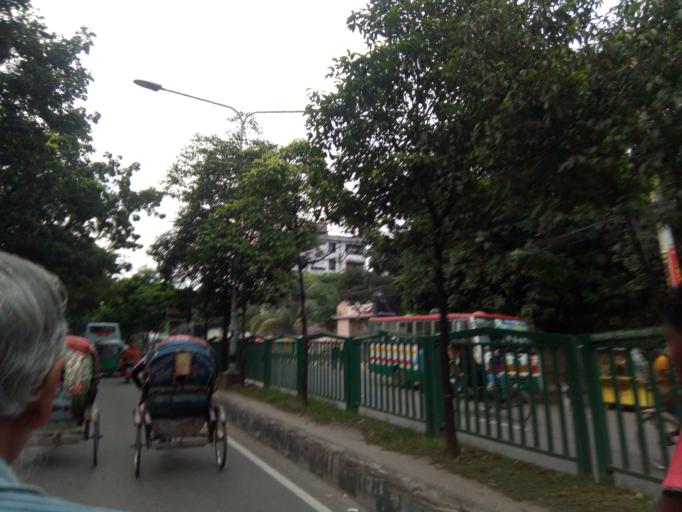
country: BD
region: Dhaka
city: Azimpur
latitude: 23.7249
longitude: 90.3869
